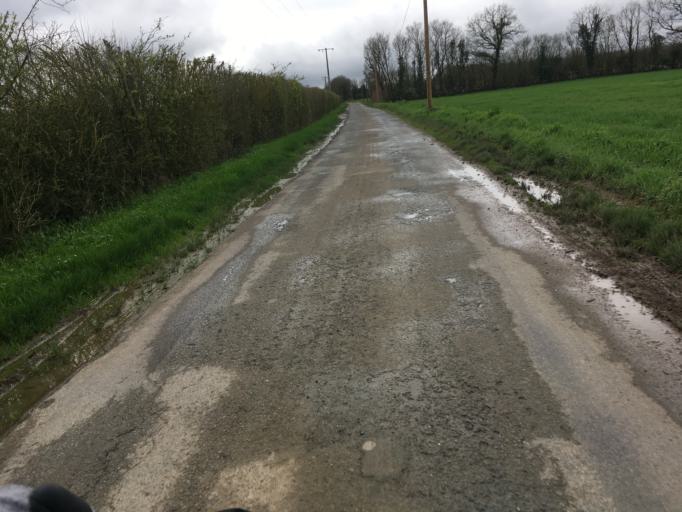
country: FR
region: Poitou-Charentes
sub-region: Departement de la Charente-Maritime
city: Saint-Germain-de-Marencennes
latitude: 46.1136
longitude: -0.7977
